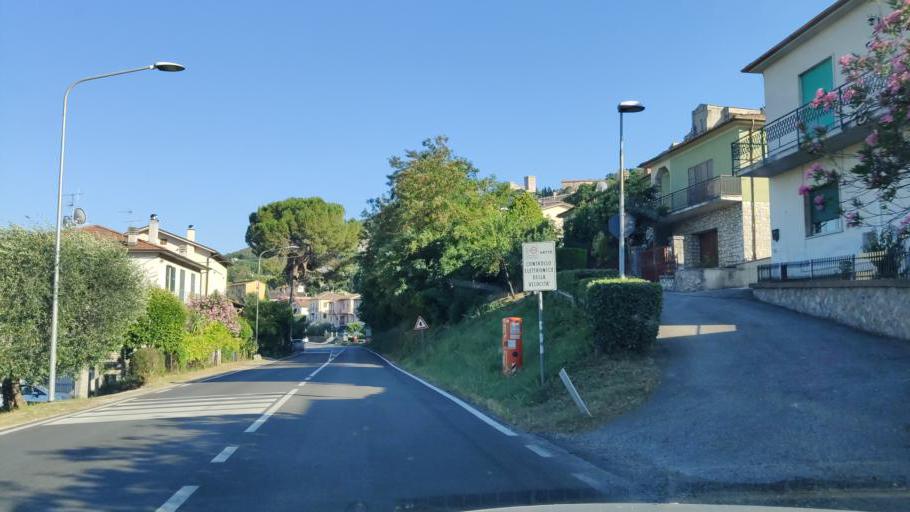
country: IT
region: Umbria
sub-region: Provincia di Terni
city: Narni
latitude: 42.5233
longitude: 12.5171
